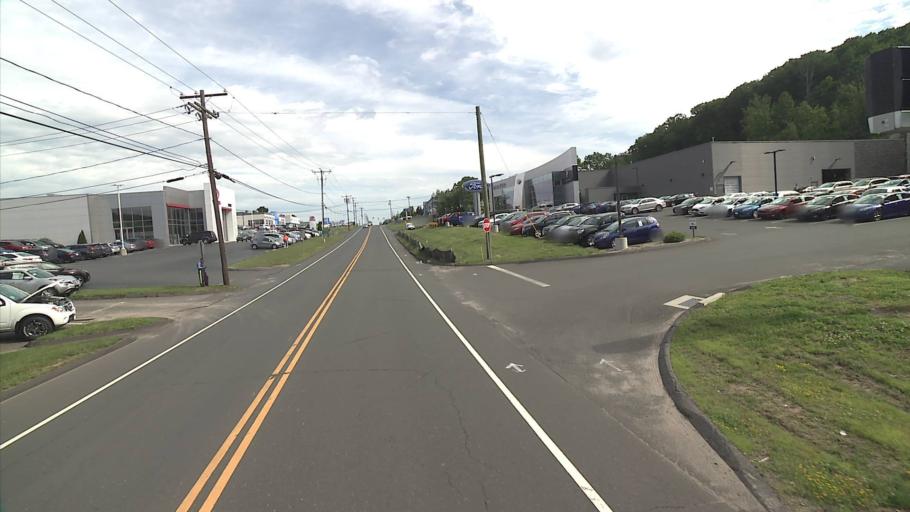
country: US
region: Connecticut
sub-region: Litchfield County
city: Oakville
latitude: 41.5682
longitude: -73.0983
